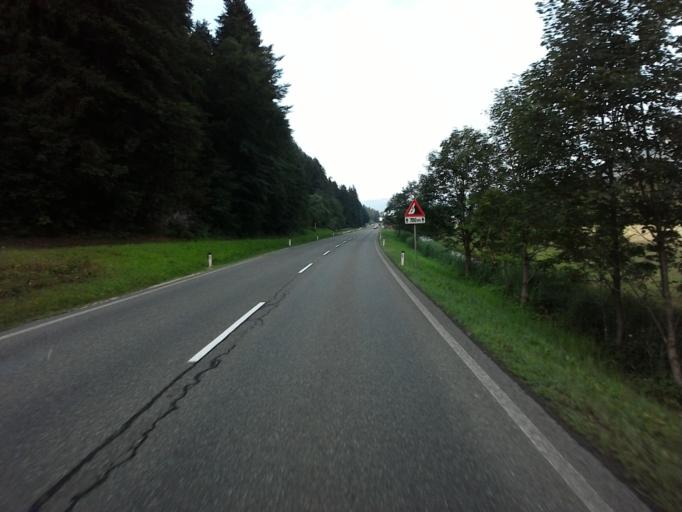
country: AT
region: Tyrol
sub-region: Politischer Bezirk Kitzbuhel
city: Kirchdorf in Tirol
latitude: 47.5630
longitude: 12.4650
